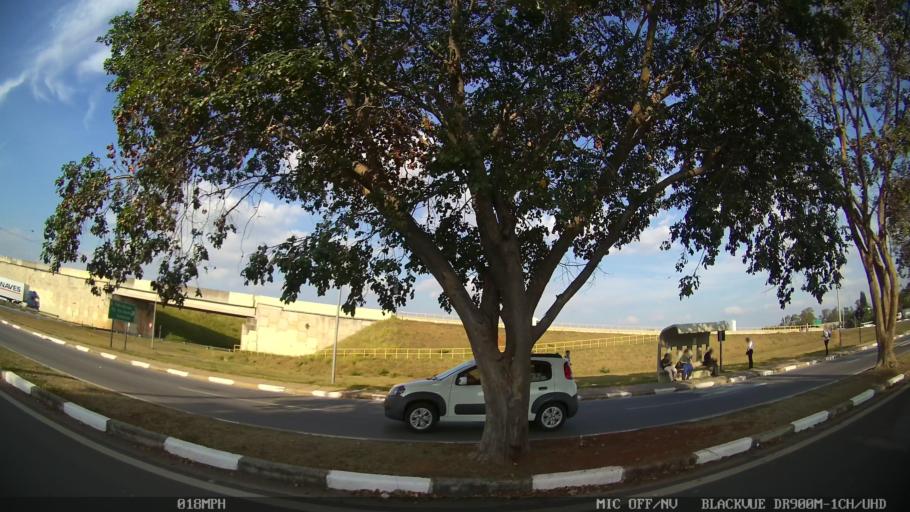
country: BR
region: Sao Paulo
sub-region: Hortolandia
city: Hortolandia
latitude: -22.8593
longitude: -47.1478
